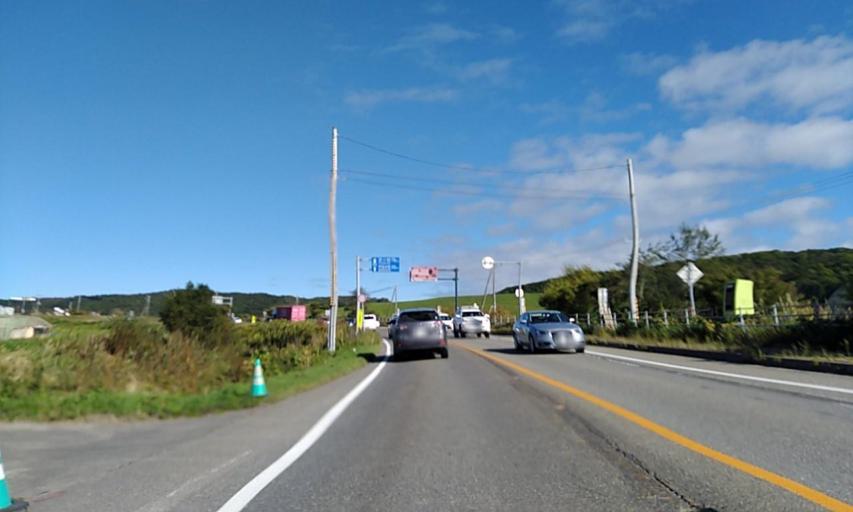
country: JP
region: Hokkaido
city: Shizunai-furukawacho
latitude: 42.3730
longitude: 142.3088
